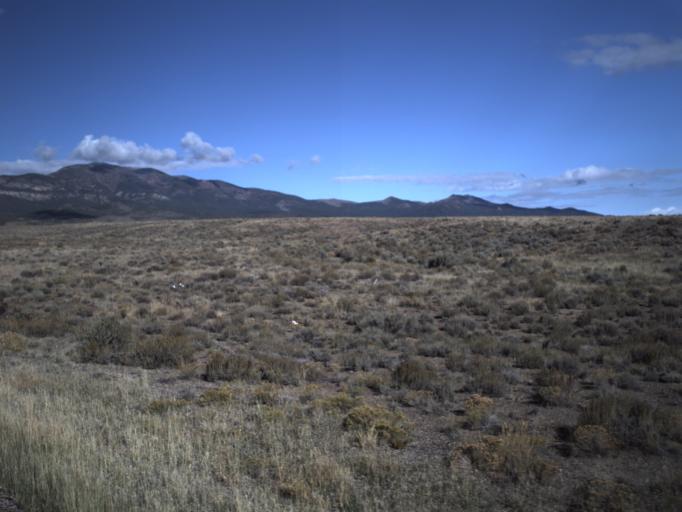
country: US
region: Utah
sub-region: Beaver County
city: Milford
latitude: 38.4483
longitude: -113.1909
